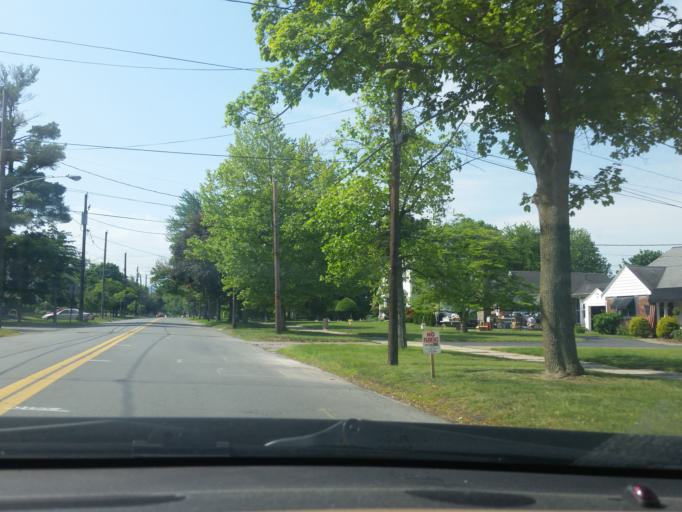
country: US
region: Pennsylvania
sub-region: Luzerne County
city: Forty Fort
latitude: 41.2764
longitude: -75.8721
